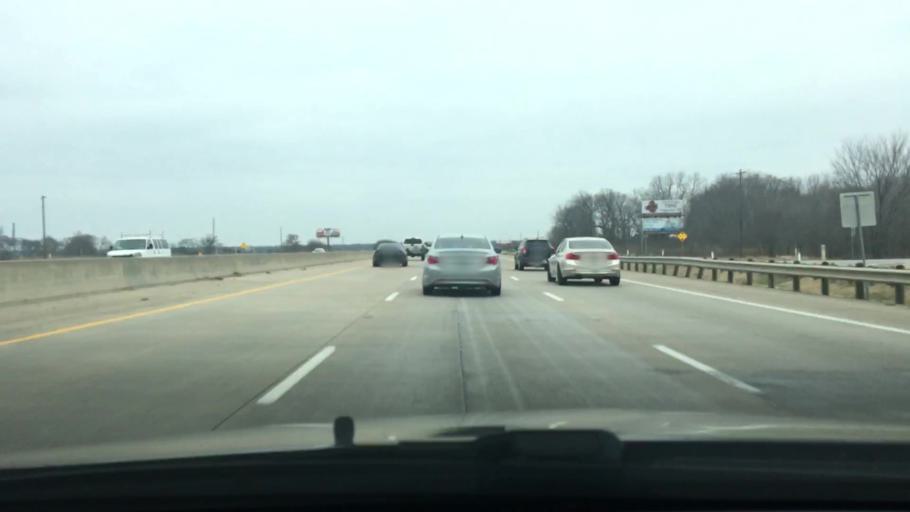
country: US
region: Texas
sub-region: Navarro County
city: Corsicana
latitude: 32.1821
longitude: -96.4717
